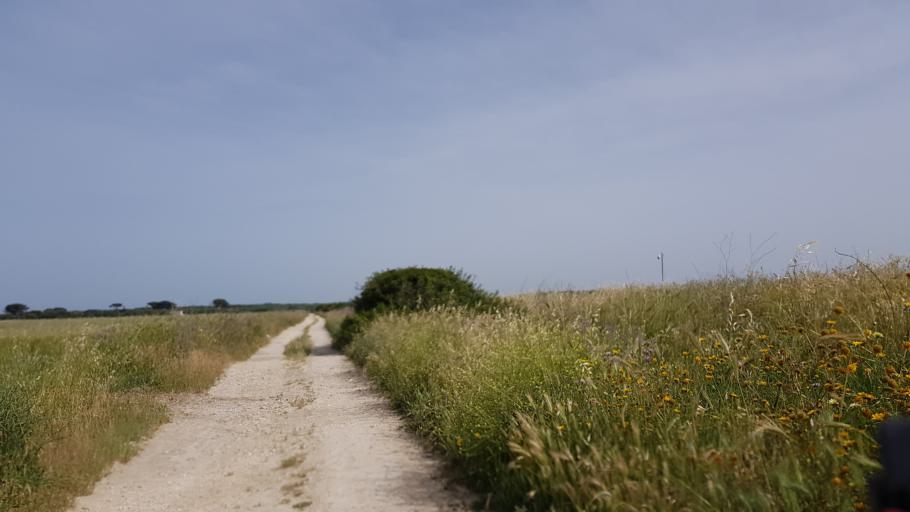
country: IT
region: Apulia
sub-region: Provincia di Brindisi
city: La Rosa
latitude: 40.5933
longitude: 17.9960
